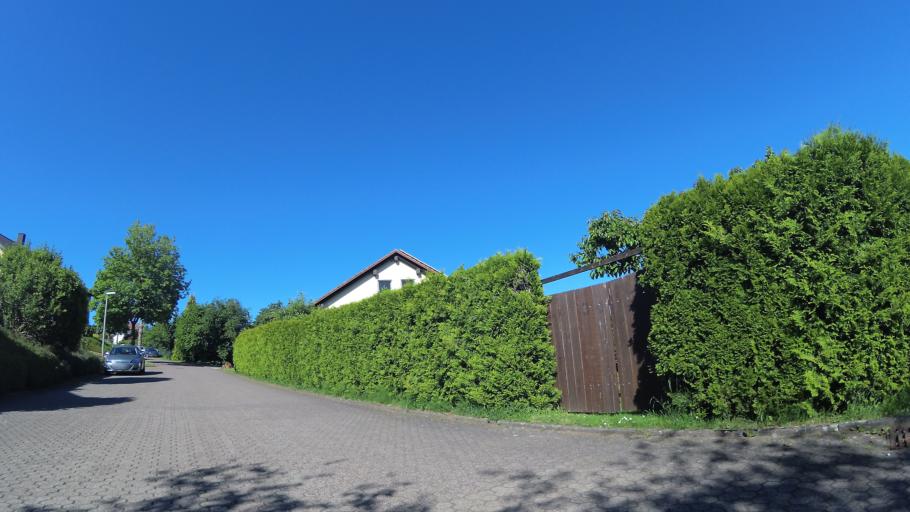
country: DE
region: Saarland
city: Marpingen
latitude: 49.4322
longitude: 7.0709
